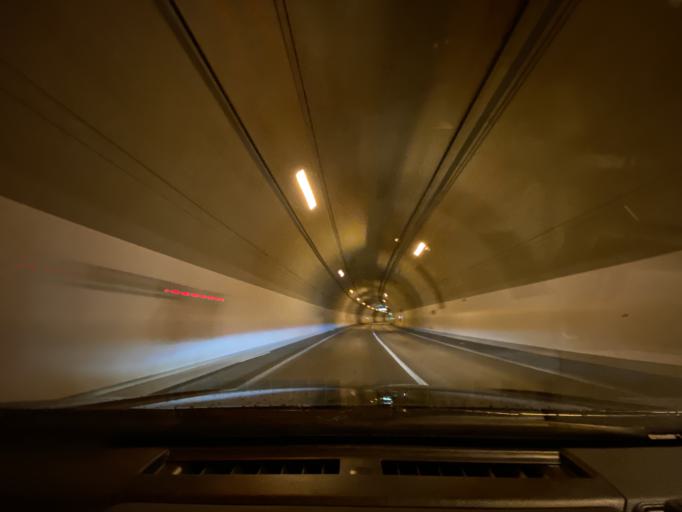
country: JP
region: Hokkaido
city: Ishikari
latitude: 43.4679
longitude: 141.3988
